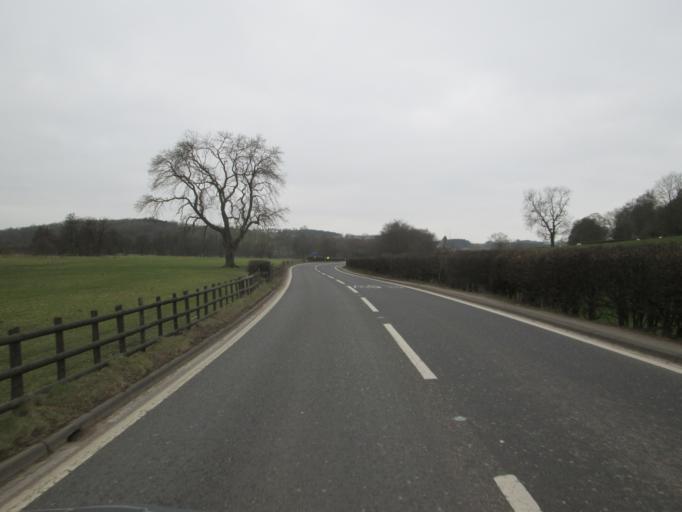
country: GB
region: England
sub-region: Derbyshire
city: Bakewell
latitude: 53.1898
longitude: -1.6334
